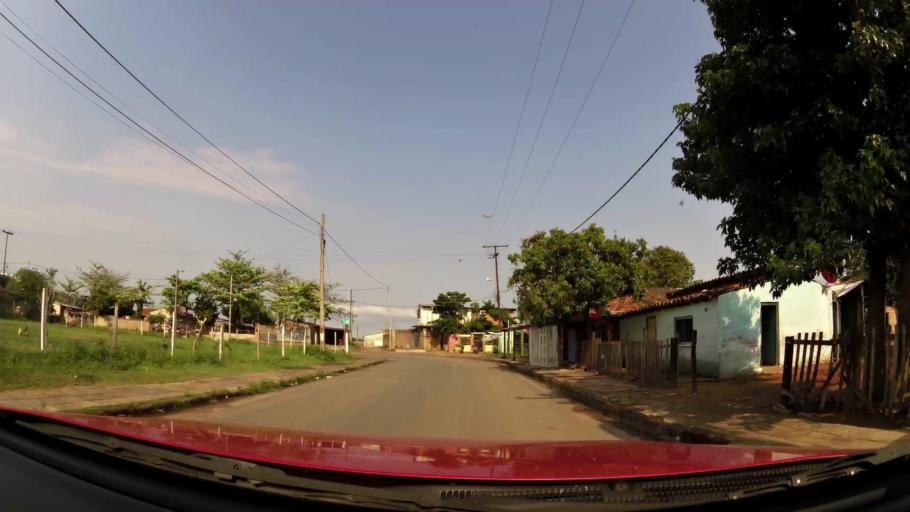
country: PY
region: Asuncion
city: Asuncion
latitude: -25.3039
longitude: -57.6679
